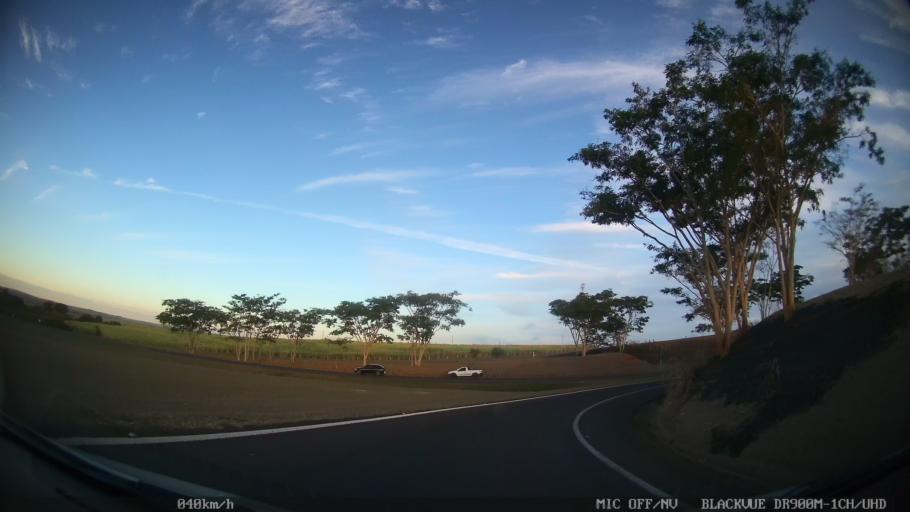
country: BR
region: Sao Paulo
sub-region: Pindorama
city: Pindorama
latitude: -21.2071
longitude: -48.9321
